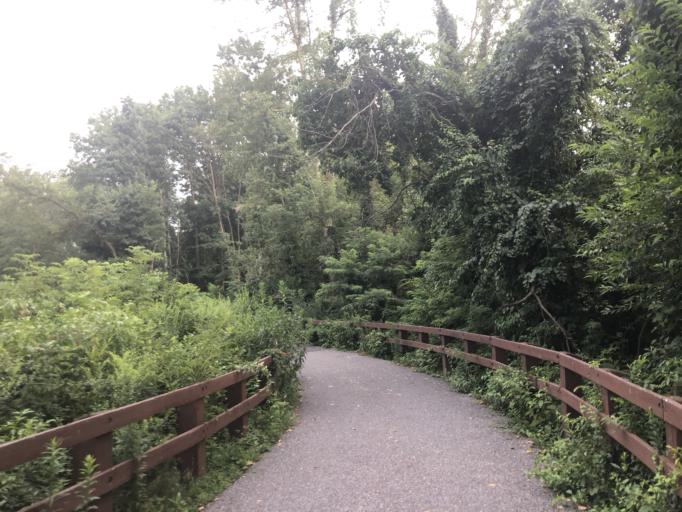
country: US
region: Maryland
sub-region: Harford County
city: Edgewood
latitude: 39.3970
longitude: -76.3501
